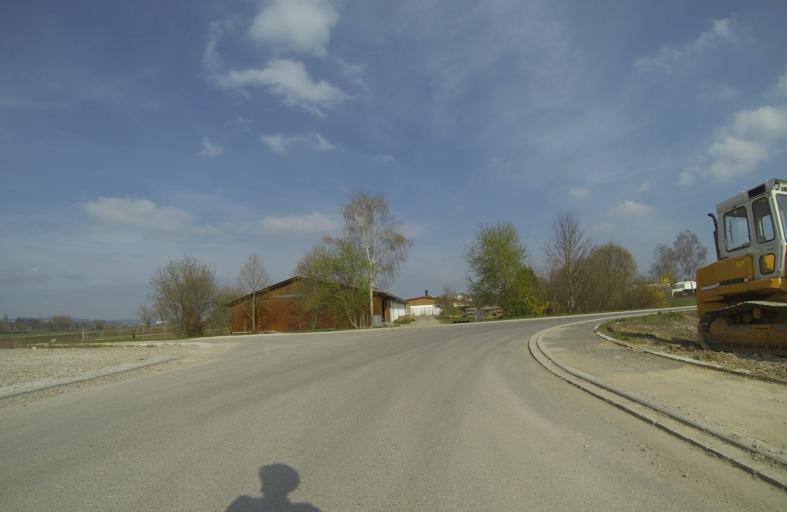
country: DE
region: Baden-Wuerttemberg
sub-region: Tuebingen Region
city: Erbach
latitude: 48.3315
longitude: 9.9072
